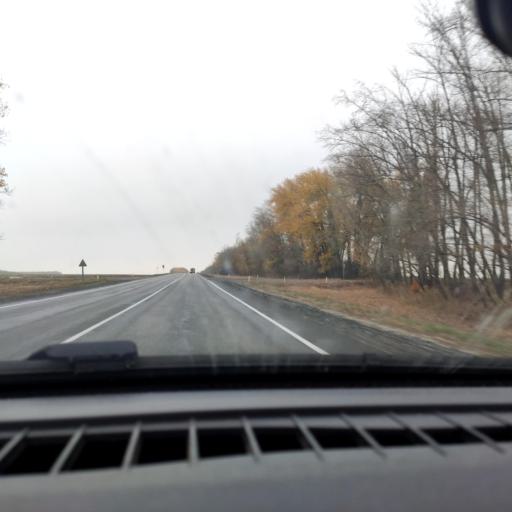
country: RU
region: Voronezj
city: Ostrogozhsk
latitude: 50.9492
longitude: 39.0507
